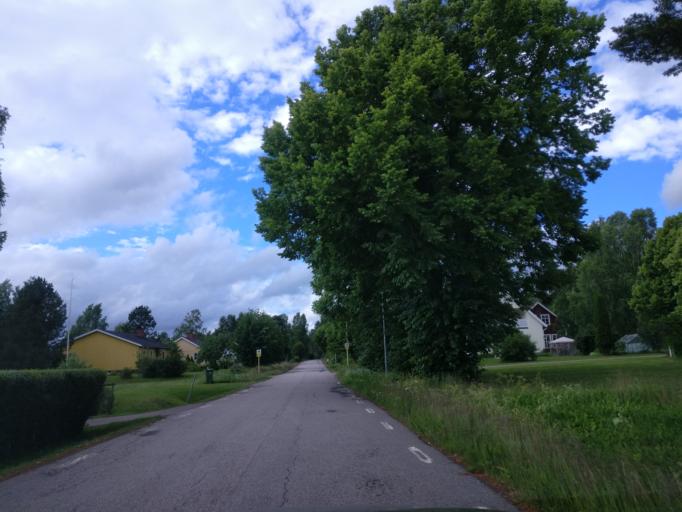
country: SE
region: Vaermland
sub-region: Munkfors Kommun
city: Munkfors
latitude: 59.9734
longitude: 13.4859
